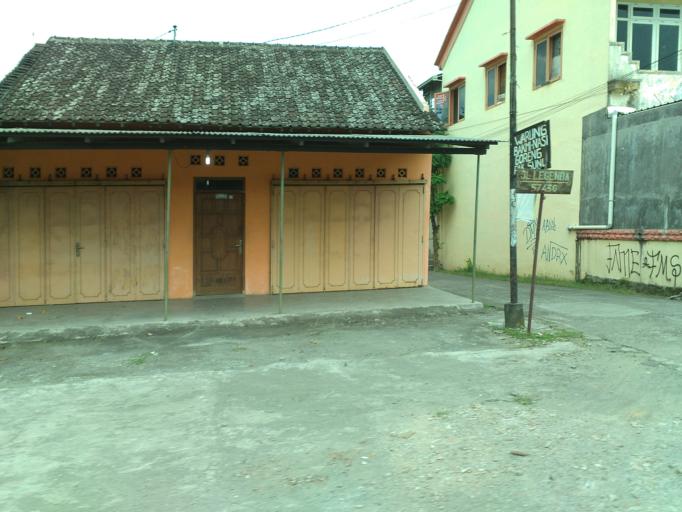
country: ID
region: Central Java
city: Klaten
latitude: -7.6895
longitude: 110.6341
